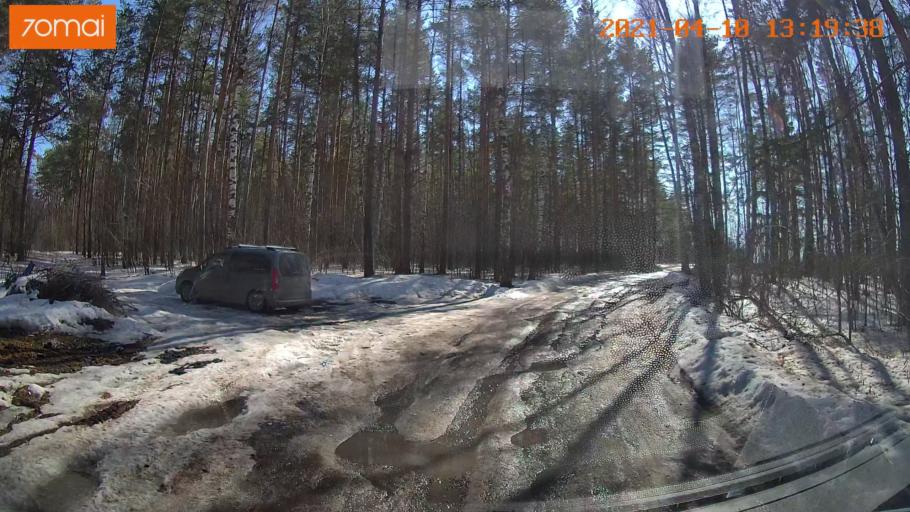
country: RU
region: Ivanovo
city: Kokhma
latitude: 56.9907
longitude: 41.0580
